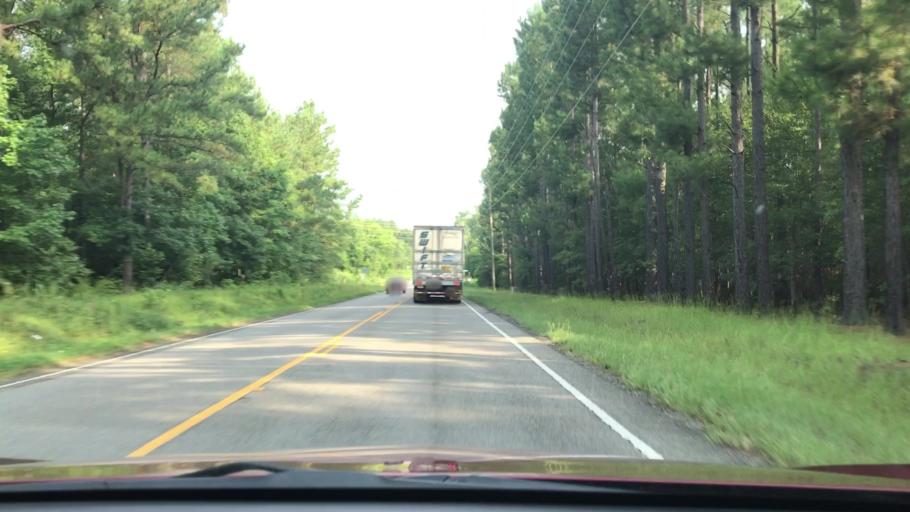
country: US
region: South Carolina
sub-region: Barnwell County
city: Blackville
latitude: 33.6023
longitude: -81.2640
